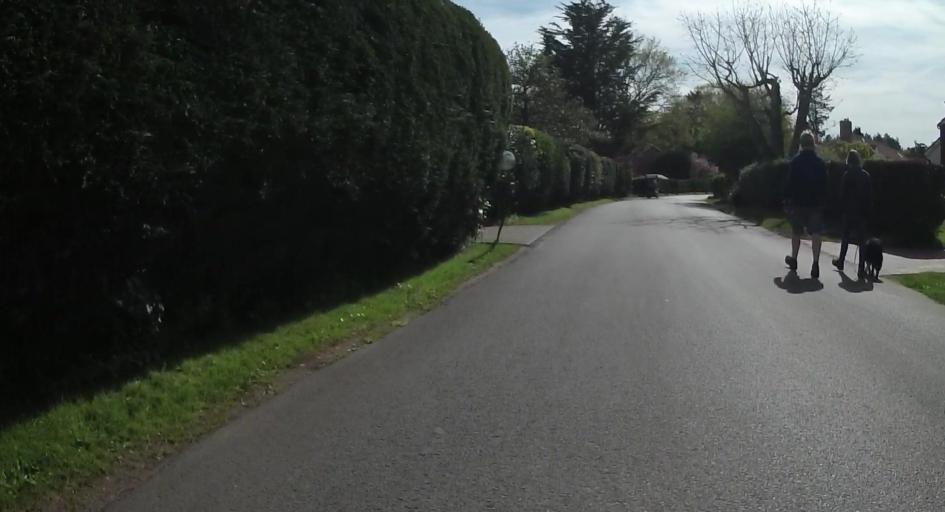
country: GB
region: England
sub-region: Surrey
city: Farnham
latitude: 51.1820
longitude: -0.8246
